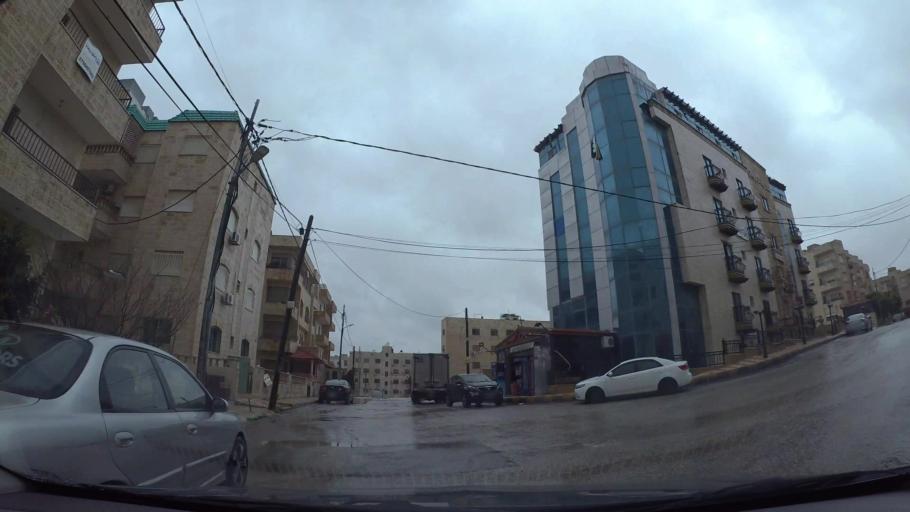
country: JO
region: Amman
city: Al Jubayhah
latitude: 32.0253
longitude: 35.8706
